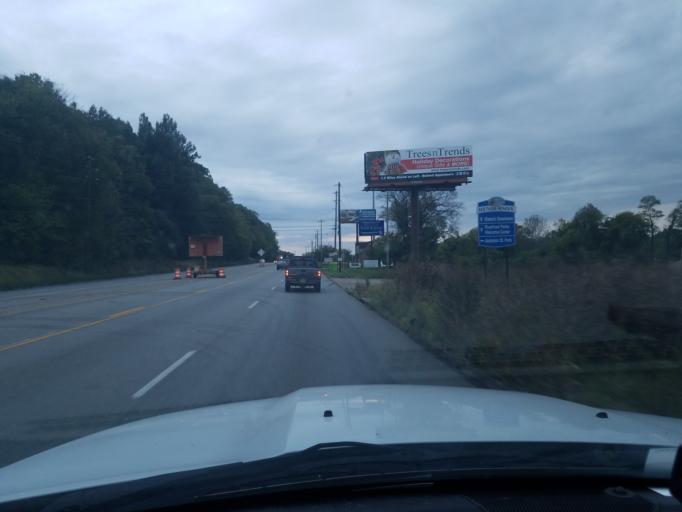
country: US
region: Kentucky
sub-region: Henderson County
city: Henderson
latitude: 37.8863
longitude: -87.5600
